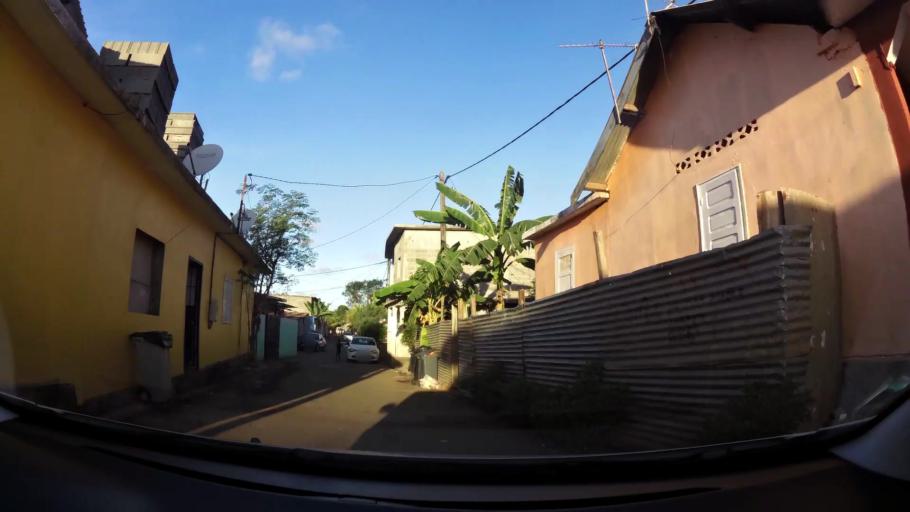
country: YT
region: Dembeni
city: Dembeni
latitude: -12.8441
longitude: 45.1849
